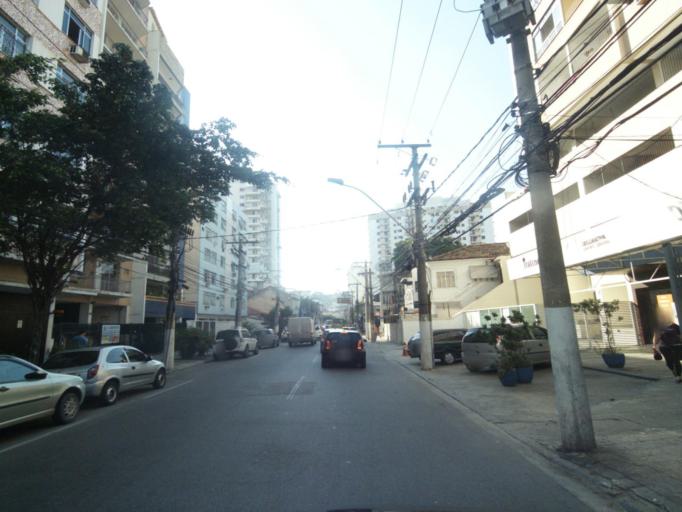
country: BR
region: Rio de Janeiro
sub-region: Niteroi
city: Niteroi
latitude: -22.9010
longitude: -43.1007
